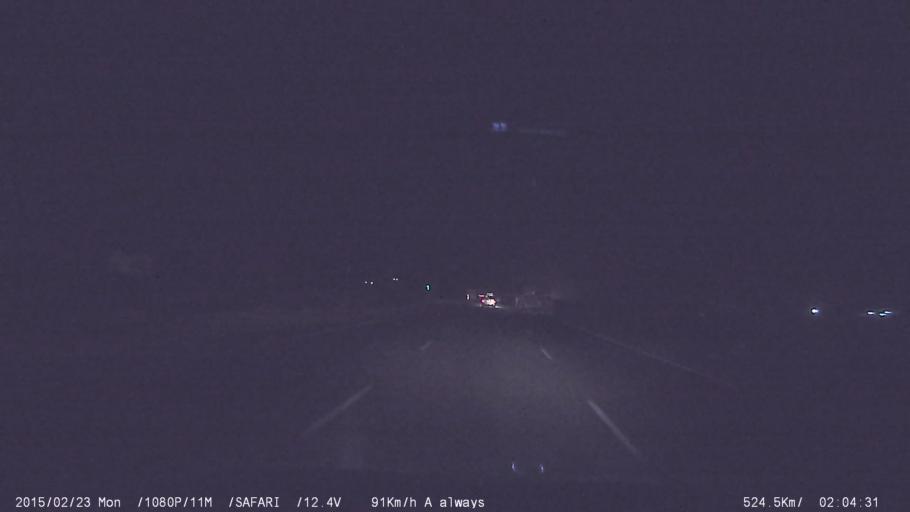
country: IN
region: Tamil Nadu
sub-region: Krishnagiri
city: Kelamangalam
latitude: 12.6483
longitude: 78.0399
